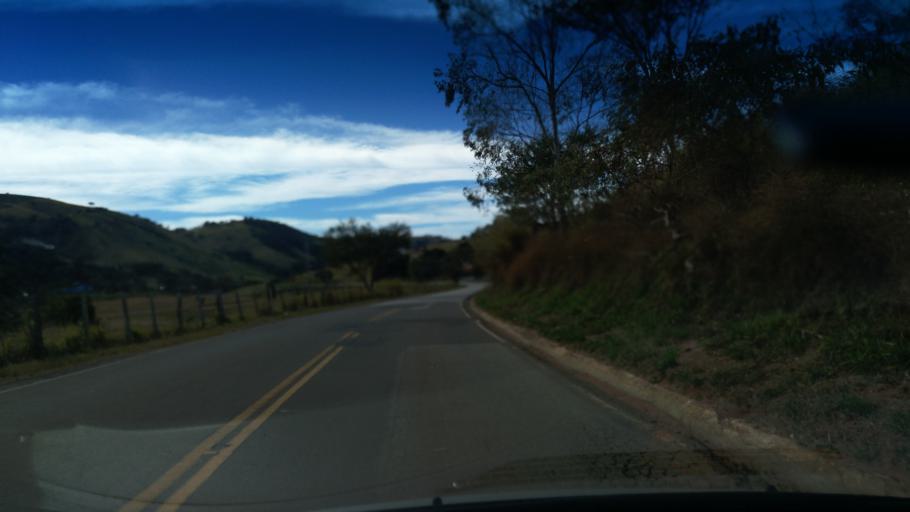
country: BR
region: Minas Gerais
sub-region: Andradas
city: Andradas
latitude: -22.0564
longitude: -46.4126
